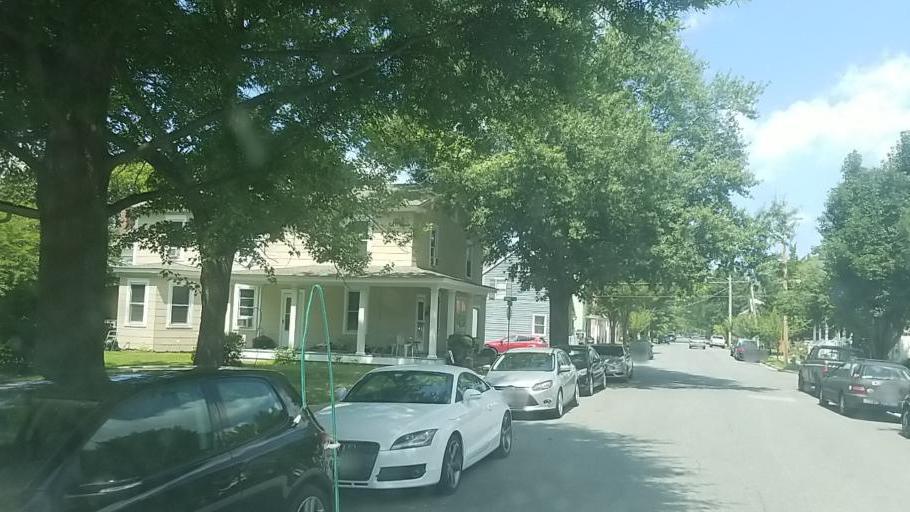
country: US
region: Maryland
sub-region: Talbot County
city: Easton
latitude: 38.7711
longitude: -76.0728
